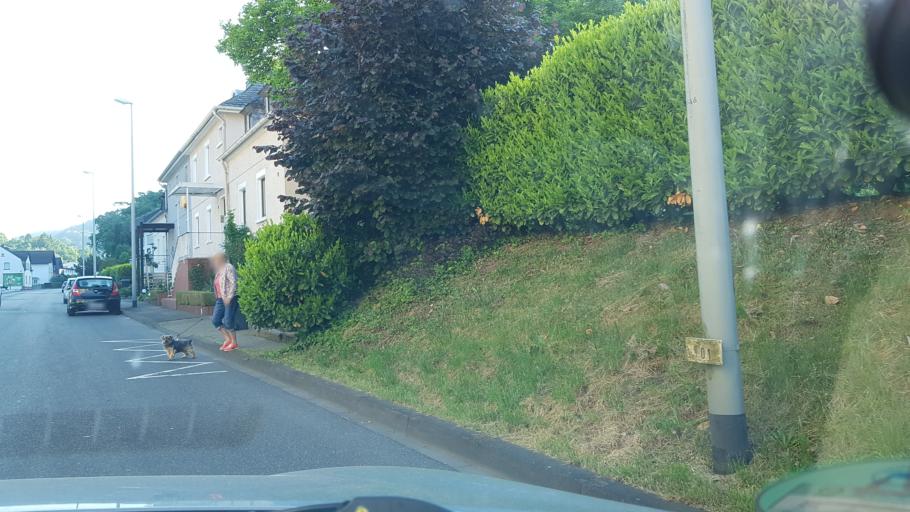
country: DE
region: Rheinland-Pfalz
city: Bad Ems
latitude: 50.3402
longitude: 7.7155
